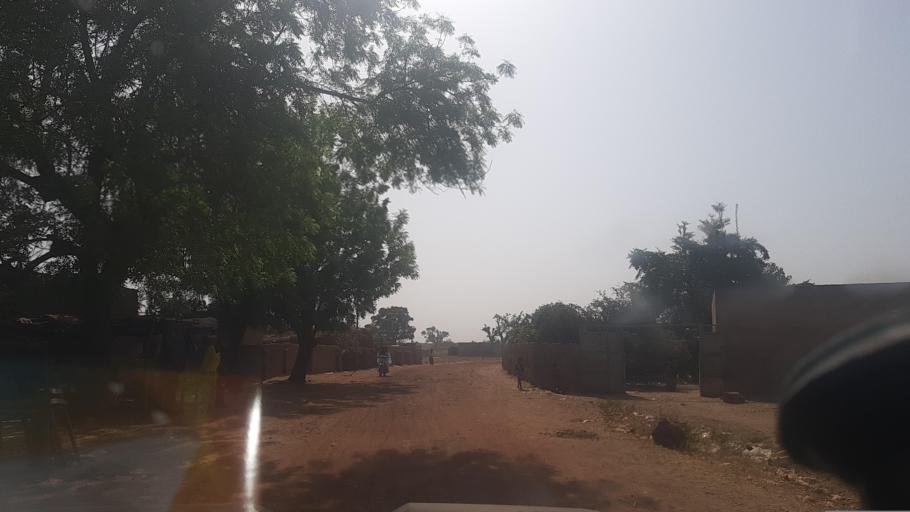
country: ML
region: Segou
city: Baroueli
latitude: 13.1655
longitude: -6.5188
